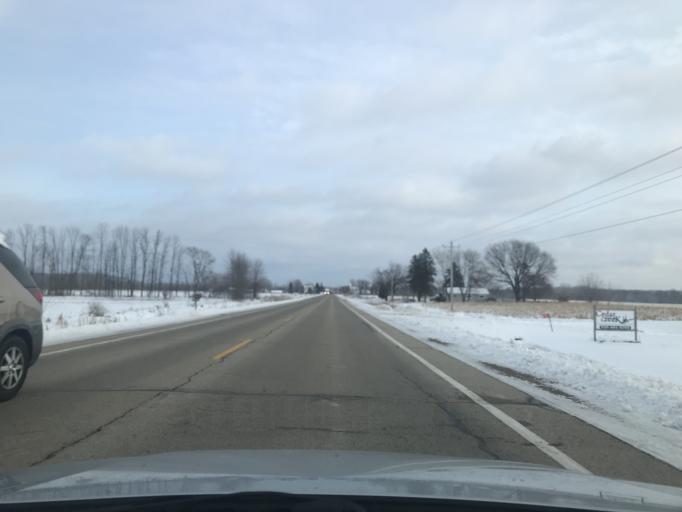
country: US
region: Wisconsin
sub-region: Oconto County
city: Oconto
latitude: 44.8925
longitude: -87.9345
